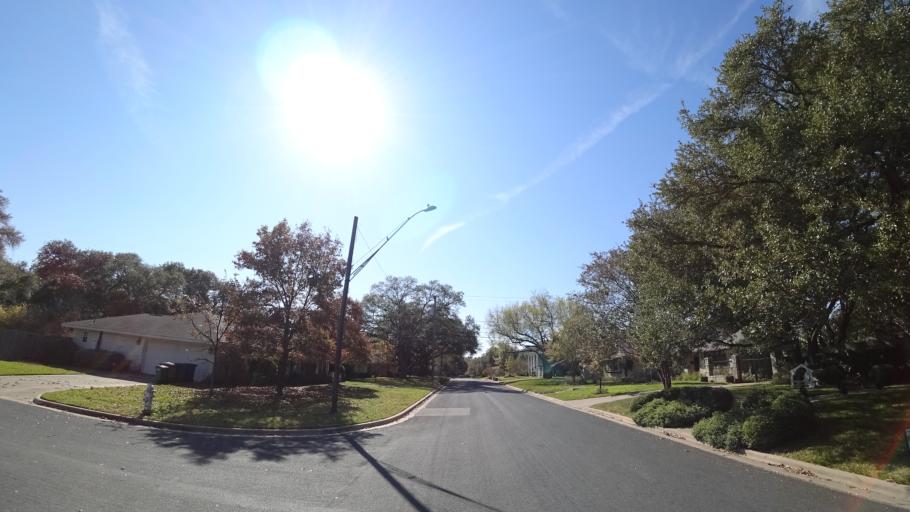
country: US
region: Texas
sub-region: Williamson County
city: Jollyville
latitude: 30.3682
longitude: -97.7632
